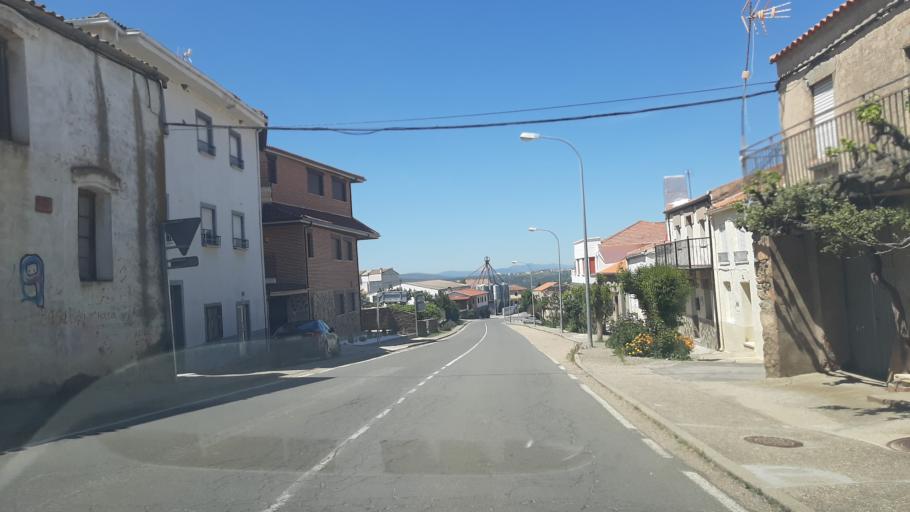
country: ES
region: Castille and Leon
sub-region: Provincia de Salamanca
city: Salvatierra de Tormes
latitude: 40.5416
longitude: -5.5799
